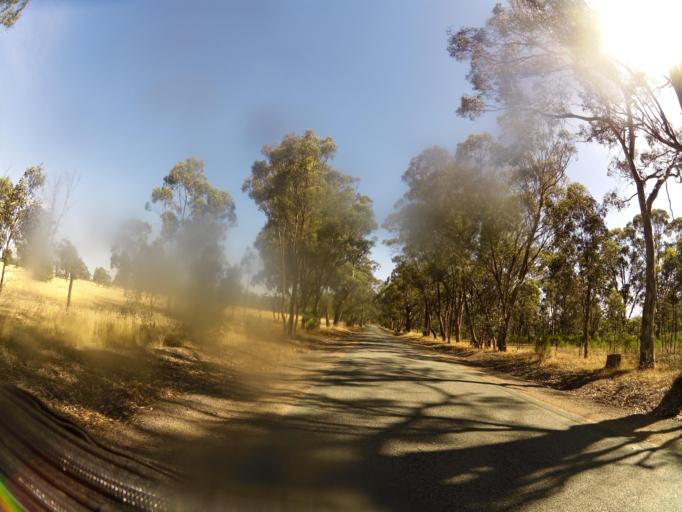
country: AU
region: Victoria
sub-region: Campaspe
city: Kyabram
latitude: -36.8739
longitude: 145.0859
